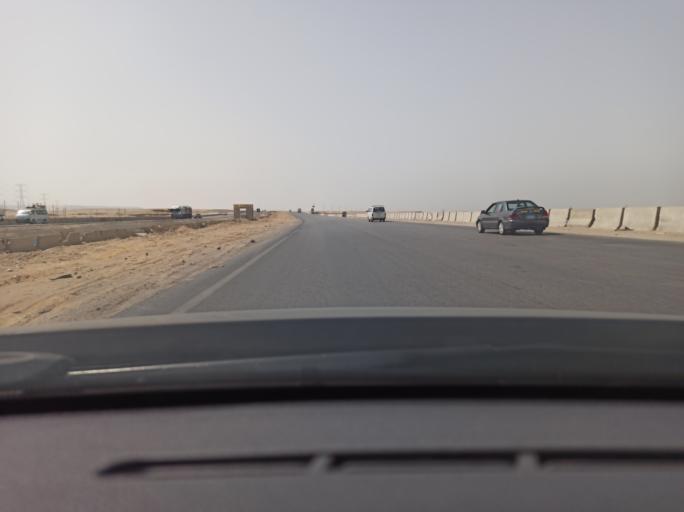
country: EG
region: Muhafazat al Fayyum
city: Al Wasitah
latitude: 29.3818
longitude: 31.3138
